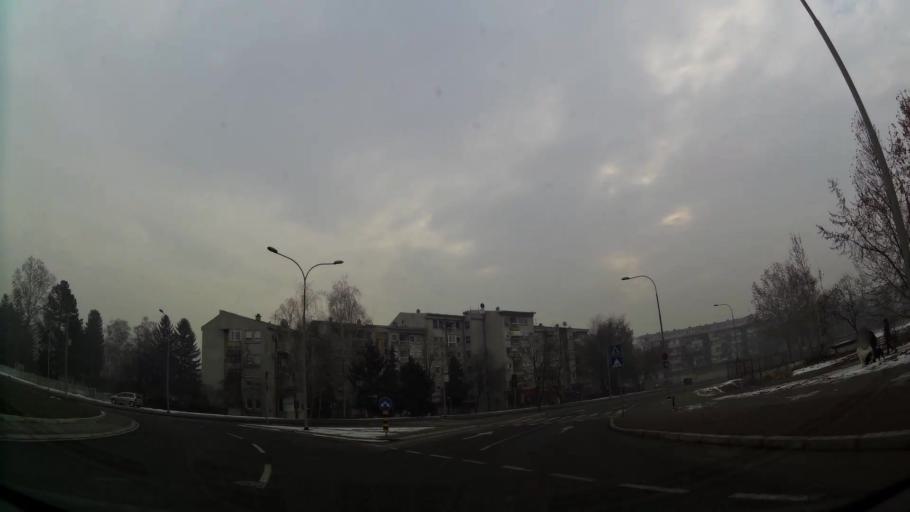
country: MK
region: Cair
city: Cair
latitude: 42.0068
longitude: 21.4631
